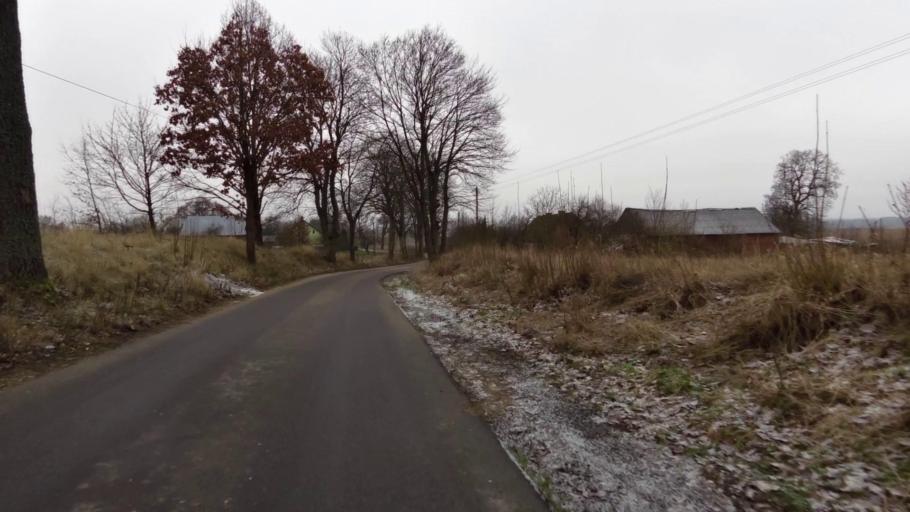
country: PL
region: West Pomeranian Voivodeship
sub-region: Powiat szczecinecki
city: Szczecinek
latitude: 53.6634
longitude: 16.6250
